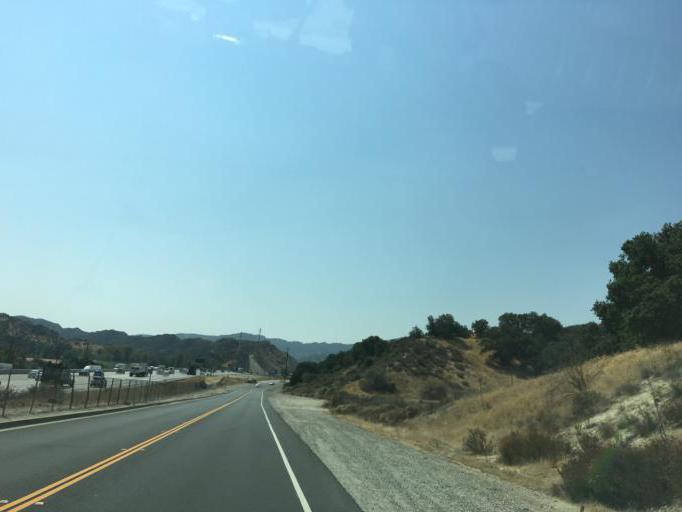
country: US
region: California
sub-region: Los Angeles County
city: Santa Clarita
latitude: 34.3682
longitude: -118.5591
